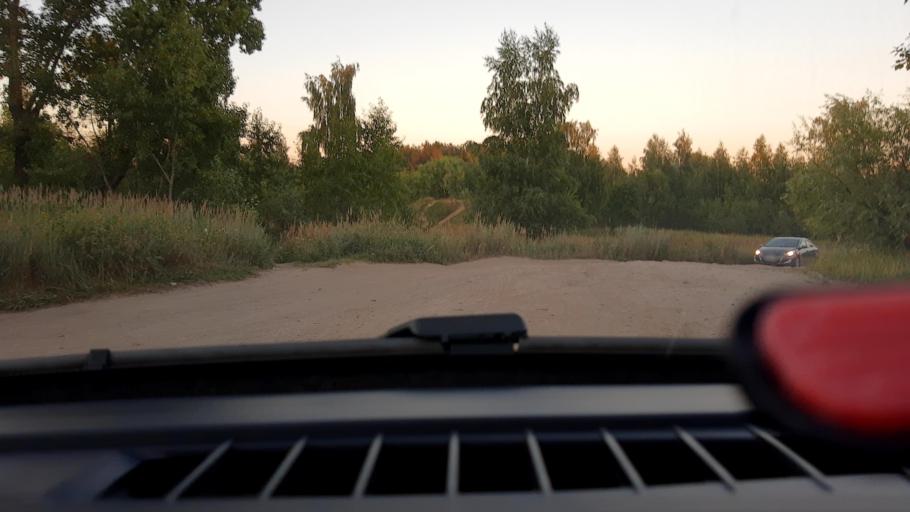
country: RU
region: Nizjnij Novgorod
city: Gorbatovka
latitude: 56.3800
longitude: 43.7753
